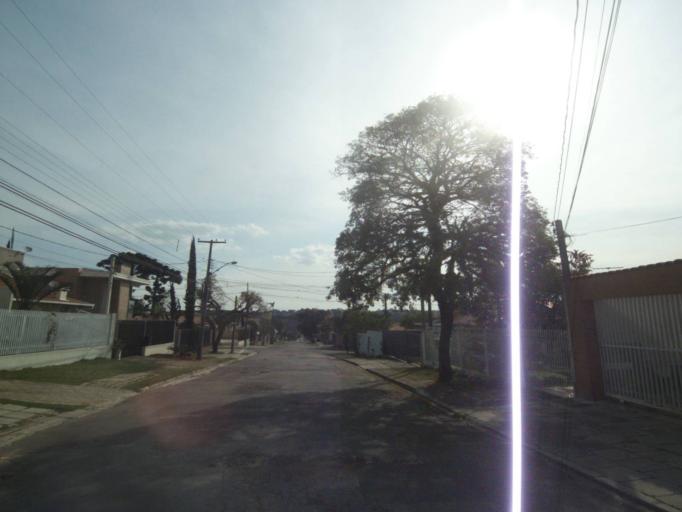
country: BR
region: Parana
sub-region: Curitiba
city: Curitiba
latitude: -25.4585
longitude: -49.3115
